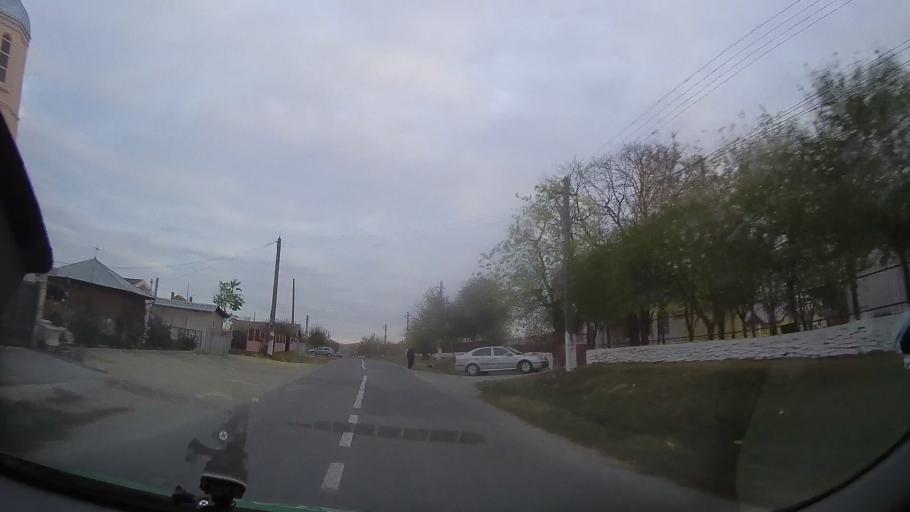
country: RO
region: Tulcea
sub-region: Comuna Mihai Bravu
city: Turda
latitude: 44.9762
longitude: 28.6208
